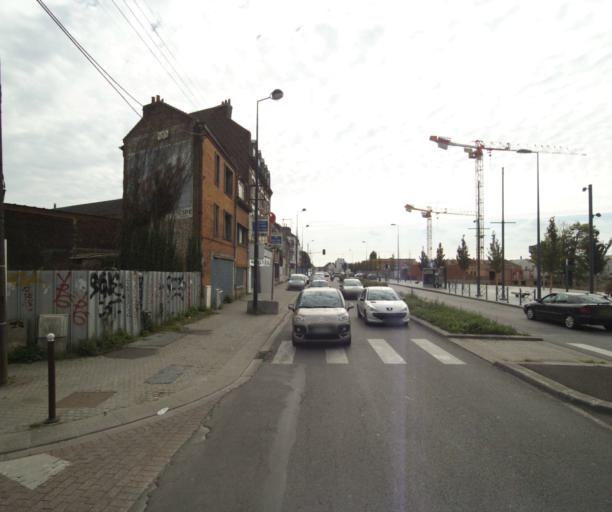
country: FR
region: Nord-Pas-de-Calais
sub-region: Departement du Nord
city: Lille
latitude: 50.6119
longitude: 3.0617
